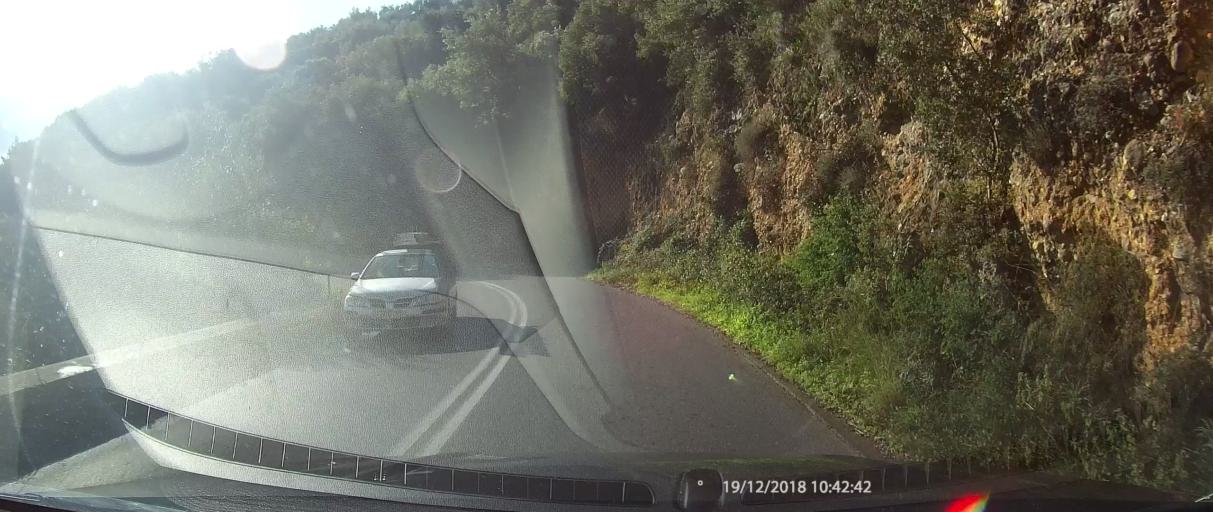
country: GR
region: Peloponnese
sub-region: Nomos Messinias
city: Paralia Vergas
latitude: 36.9535
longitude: 22.1927
